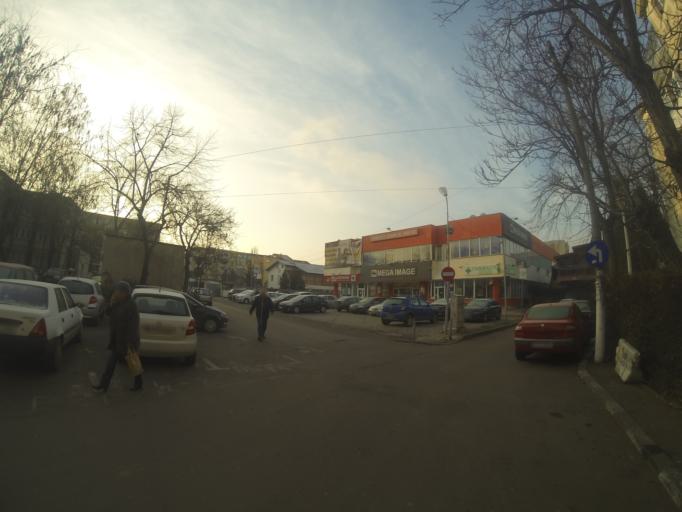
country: RO
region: Bucuresti
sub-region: Municipiul Bucuresti
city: Bucuresti
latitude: 44.4094
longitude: 26.0706
